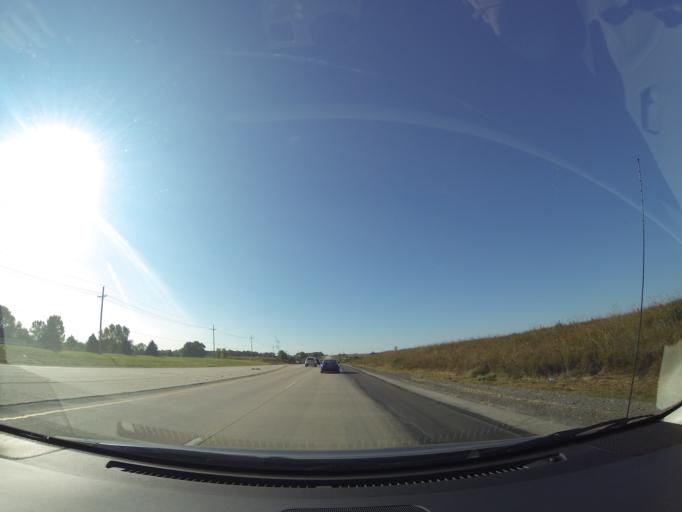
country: US
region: Nebraska
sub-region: Douglas County
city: Elkhorn
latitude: 41.2174
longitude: -96.2345
